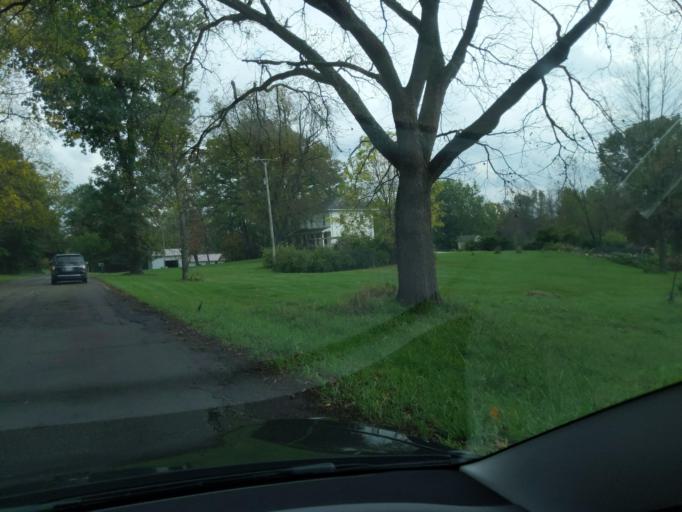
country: US
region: Michigan
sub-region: Ingham County
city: Leslie
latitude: 42.4121
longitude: -84.3801
